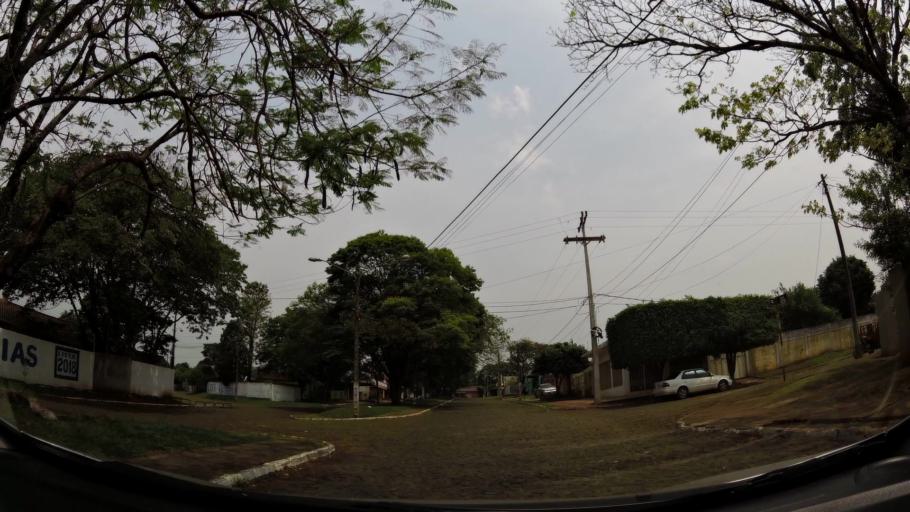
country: PY
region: Alto Parana
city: Presidente Franco
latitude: -25.5556
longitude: -54.6147
